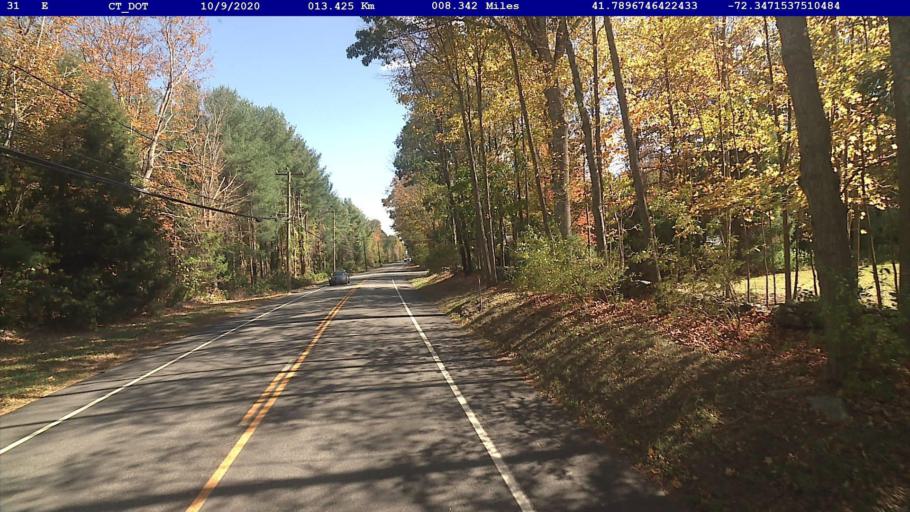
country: US
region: Connecticut
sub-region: Tolland County
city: Coventry Lake
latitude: 41.7897
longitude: -72.3471
